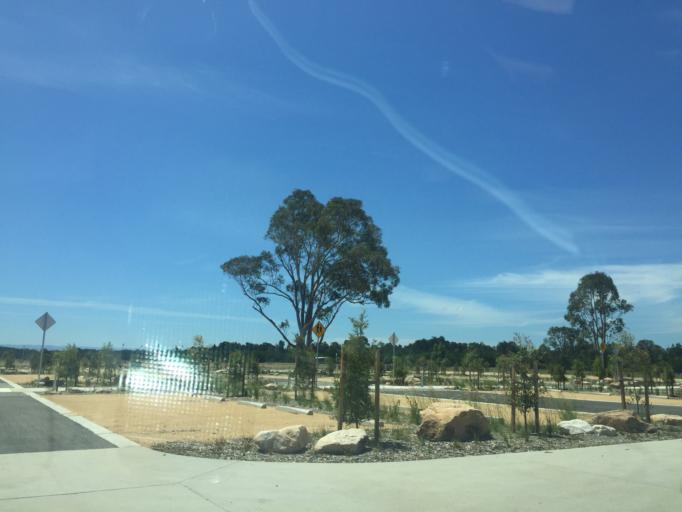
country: AU
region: New South Wales
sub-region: Blacktown
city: Doonside
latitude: -33.7860
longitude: 150.8712
